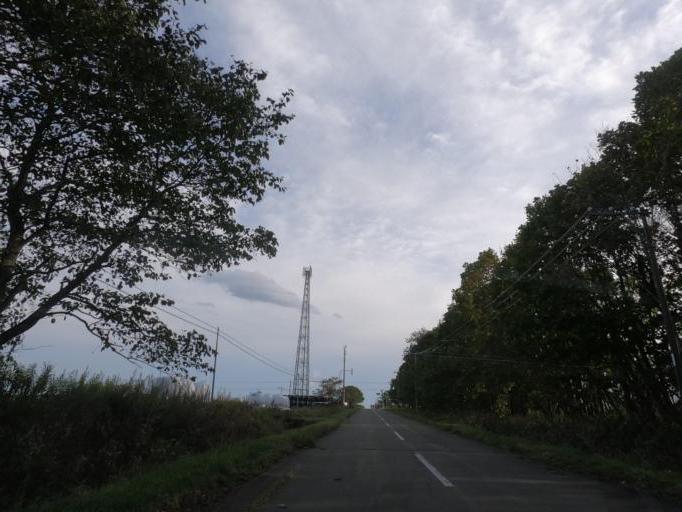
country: JP
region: Hokkaido
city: Obihiro
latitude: 42.5002
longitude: 143.4173
